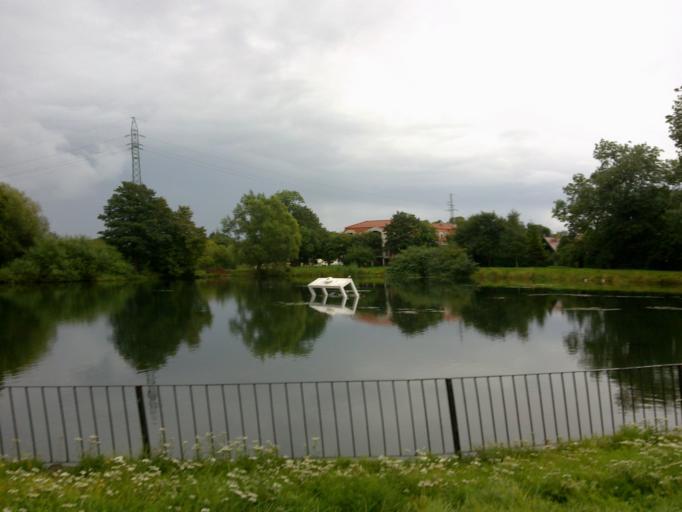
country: PL
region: Pomeranian Voivodeship
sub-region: Sopot
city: Sopot
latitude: 54.4132
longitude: 18.5668
